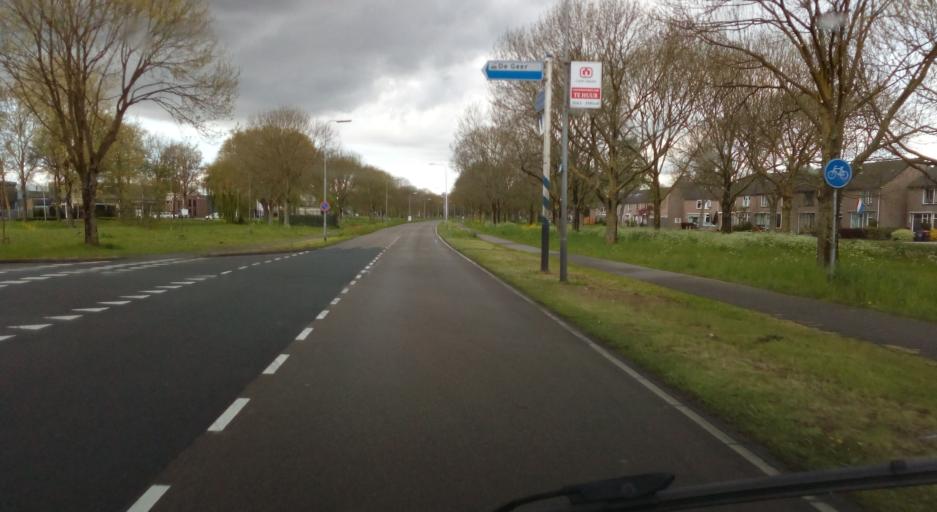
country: NL
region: South Holland
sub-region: Gemeente Zwijndrecht
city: Zwijndrecht
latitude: 51.8125
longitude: 4.6060
